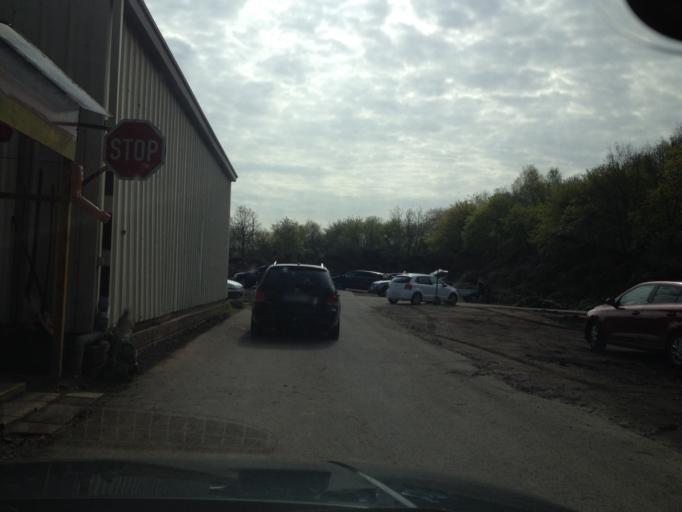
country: DE
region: Saarland
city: Sankt Wendel
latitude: 49.4469
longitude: 7.1655
